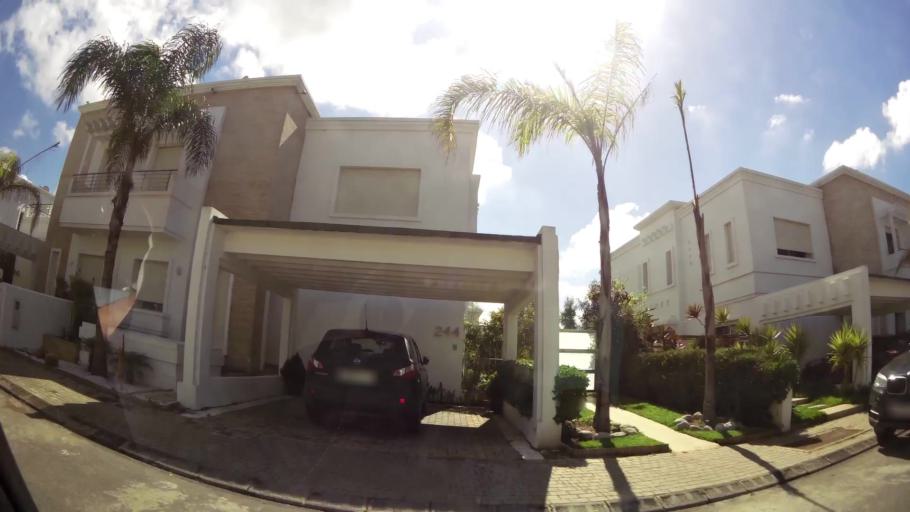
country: MA
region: Grand Casablanca
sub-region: Nouaceur
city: Bouskoura
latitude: 33.4692
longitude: -7.5973
